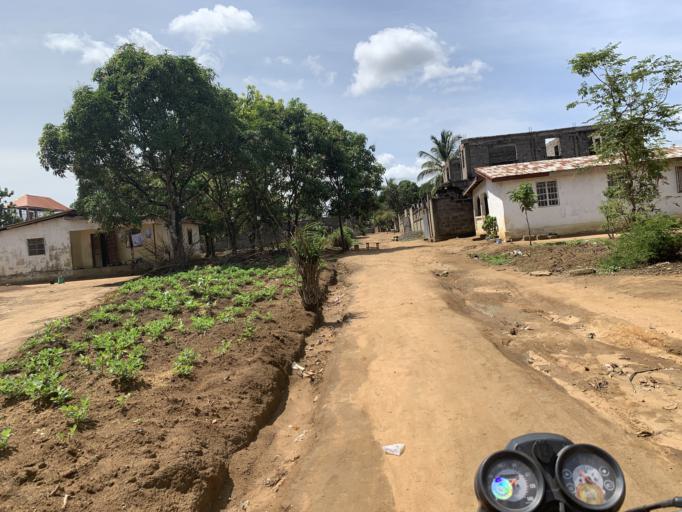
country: SL
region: Western Area
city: Waterloo
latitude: 8.3374
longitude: -13.0520
